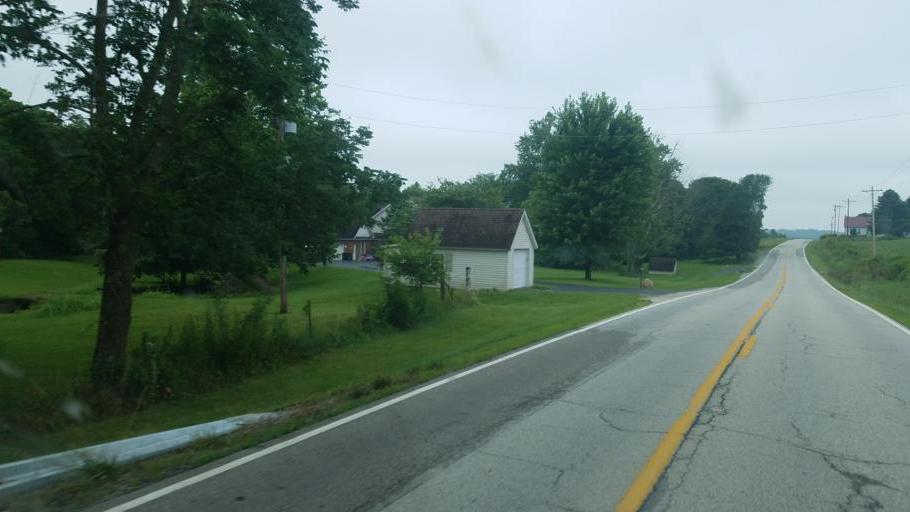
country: US
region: Ohio
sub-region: Highland County
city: Hillsboro
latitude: 39.2384
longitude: -83.5706
